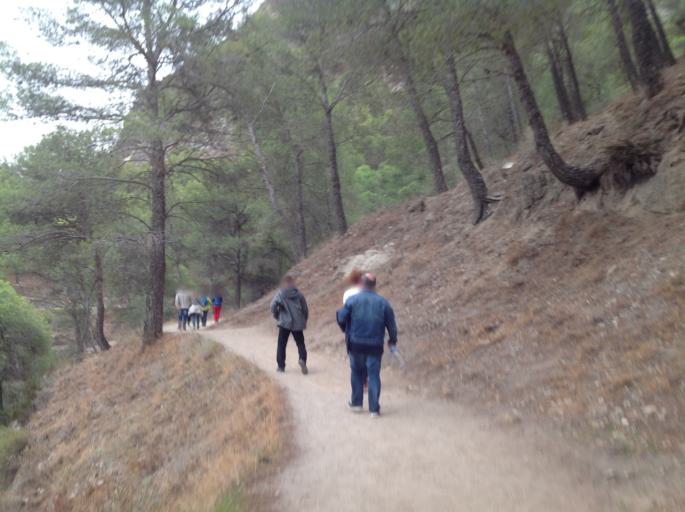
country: ES
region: Andalusia
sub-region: Provincia de Malaga
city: Ardales
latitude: 36.9295
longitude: -4.7980
